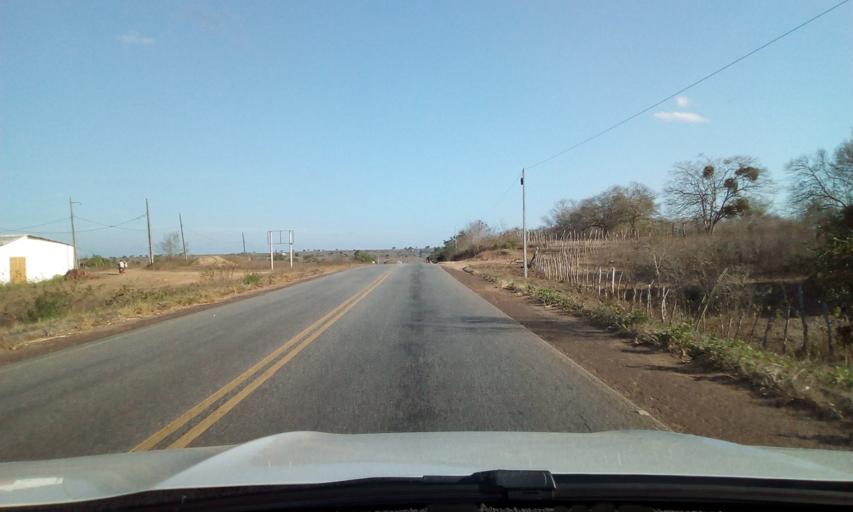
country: BR
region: Paraiba
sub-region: Mulungu
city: Mulungu
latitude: -6.9627
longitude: -35.4100
